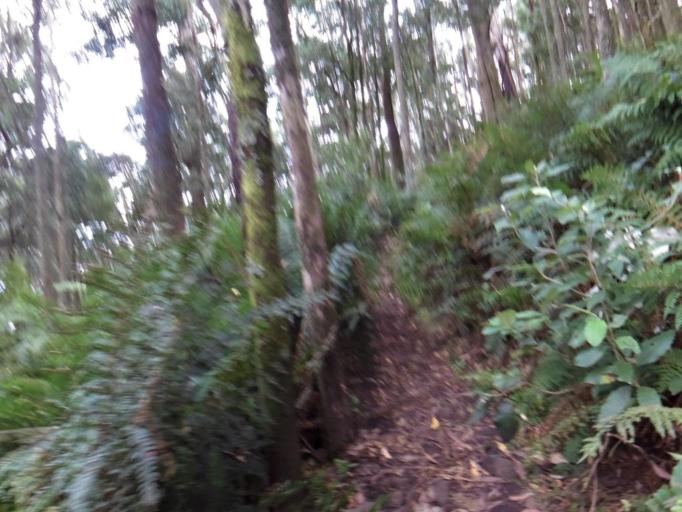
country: AU
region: Victoria
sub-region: Hume
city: Sunbury
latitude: -37.3927
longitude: 144.5769
